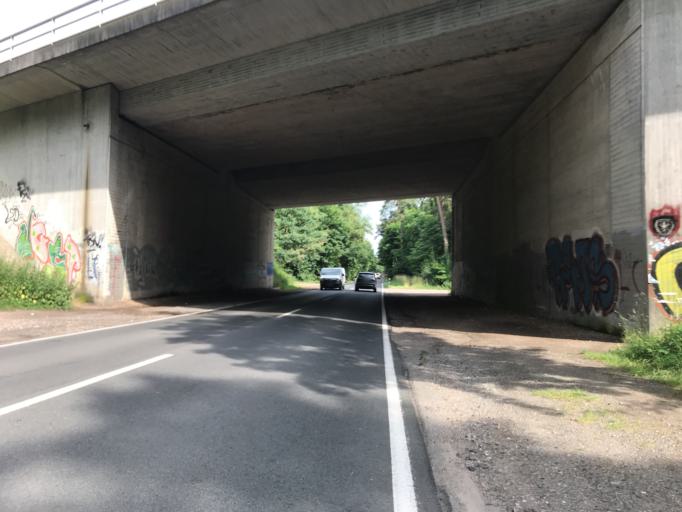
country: DE
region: Rheinland-Pfalz
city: Budenheim
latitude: 50.0049
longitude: 8.1896
